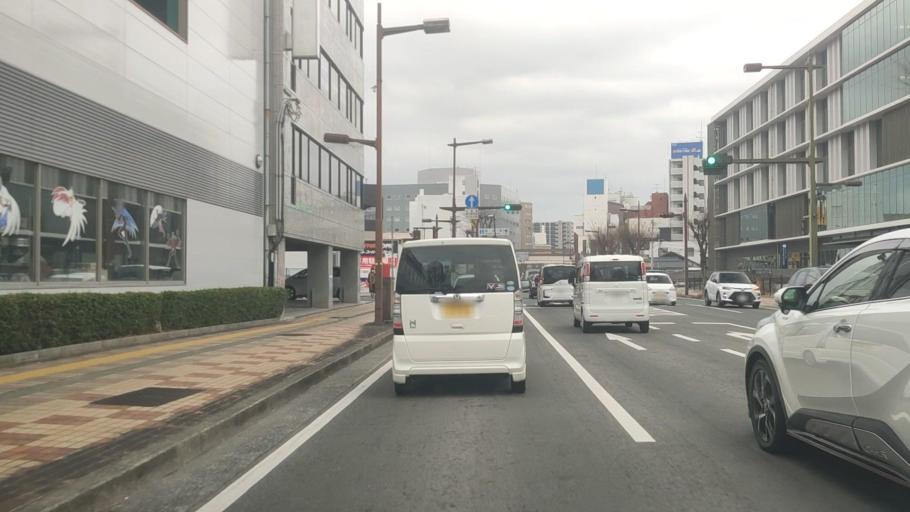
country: JP
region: Kumamoto
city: Kumamoto
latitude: 32.8015
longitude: 130.7190
